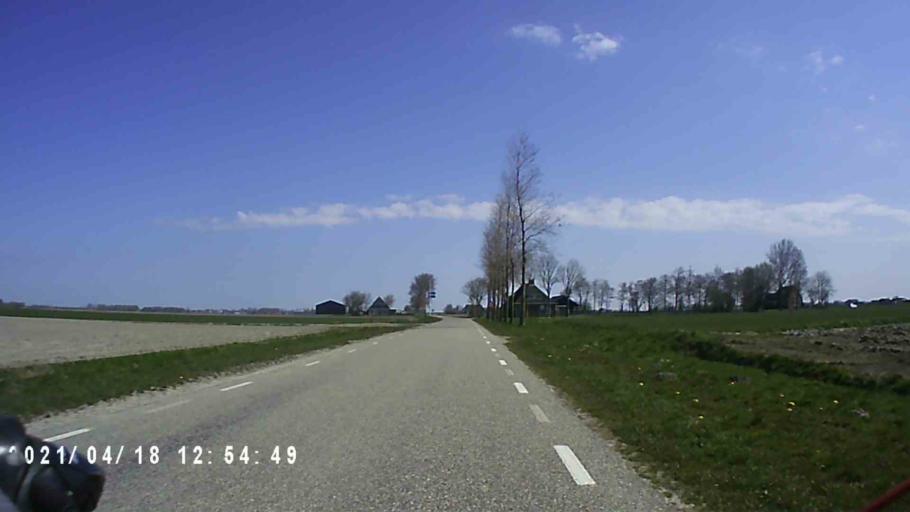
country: NL
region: Friesland
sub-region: Gemeente Dongeradeel
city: Anjum
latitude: 53.3859
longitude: 6.0713
